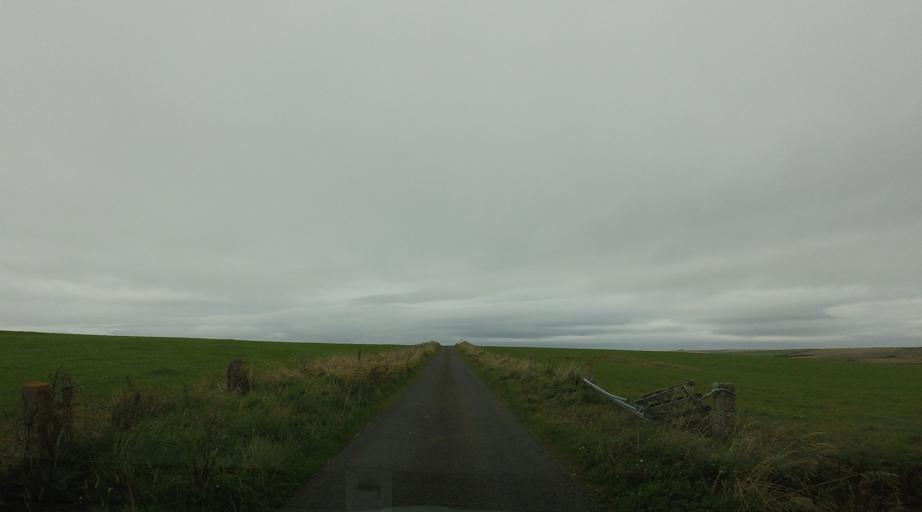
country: GB
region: Scotland
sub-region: Orkney Islands
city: Orkney
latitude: 58.7999
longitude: -2.9516
